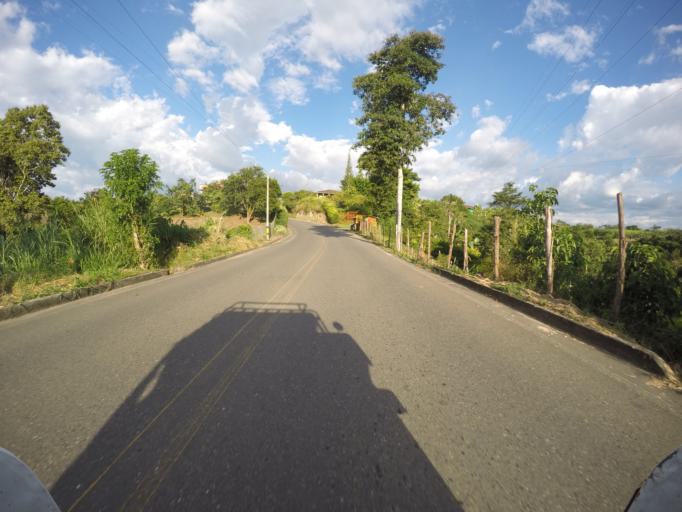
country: CO
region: Valle del Cauca
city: Alcala
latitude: 4.6863
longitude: -75.8130
